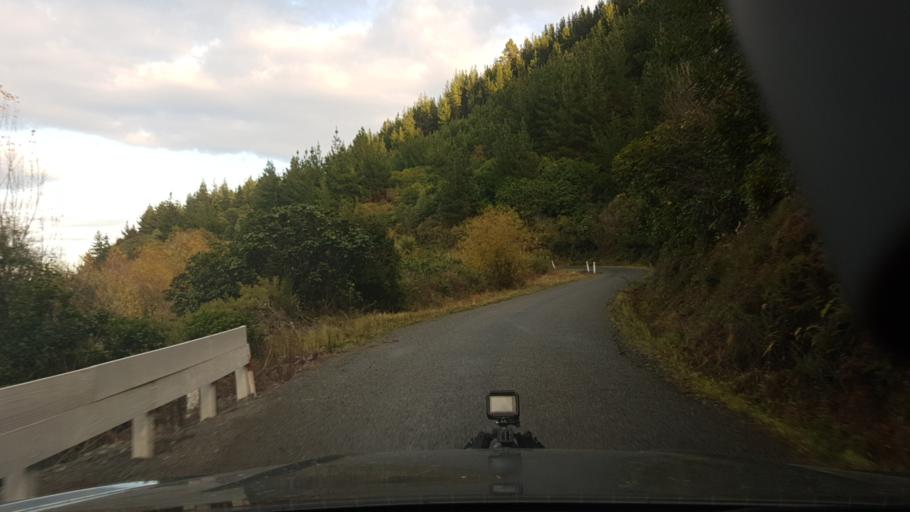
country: NZ
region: Nelson
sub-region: Nelson City
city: Nelson
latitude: -41.5796
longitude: 173.4277
